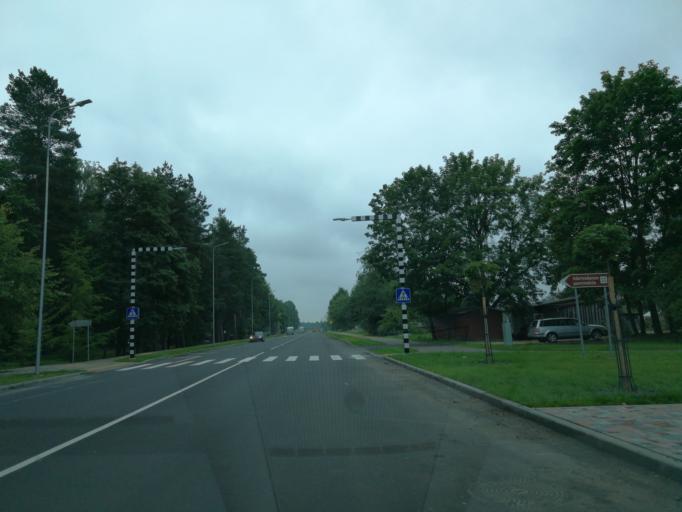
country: LV
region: Livani
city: Livani
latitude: 56.3533
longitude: 26.1811
